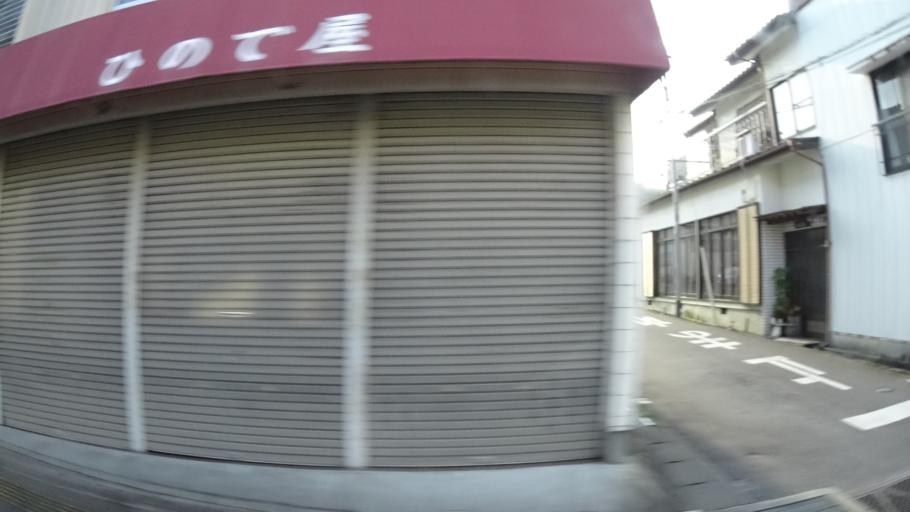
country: JP
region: Tochigi
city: Karasuyama
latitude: 36.6494
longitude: 140.1521
